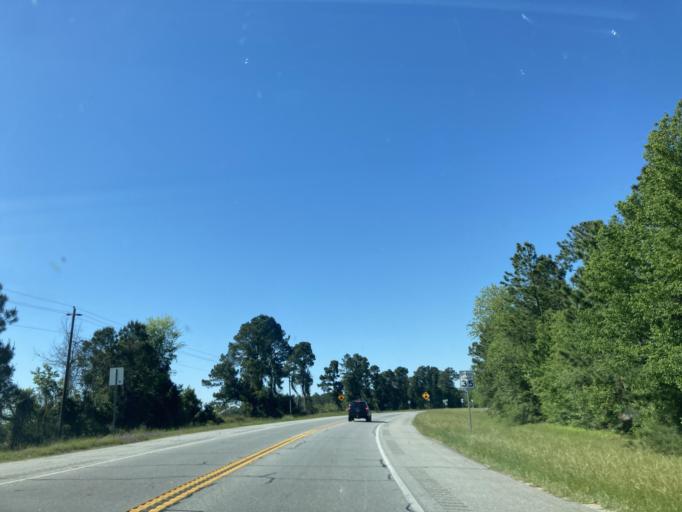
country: US
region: Georgia
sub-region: Baker County
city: Newton
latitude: 31.3079
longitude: -84.3472
